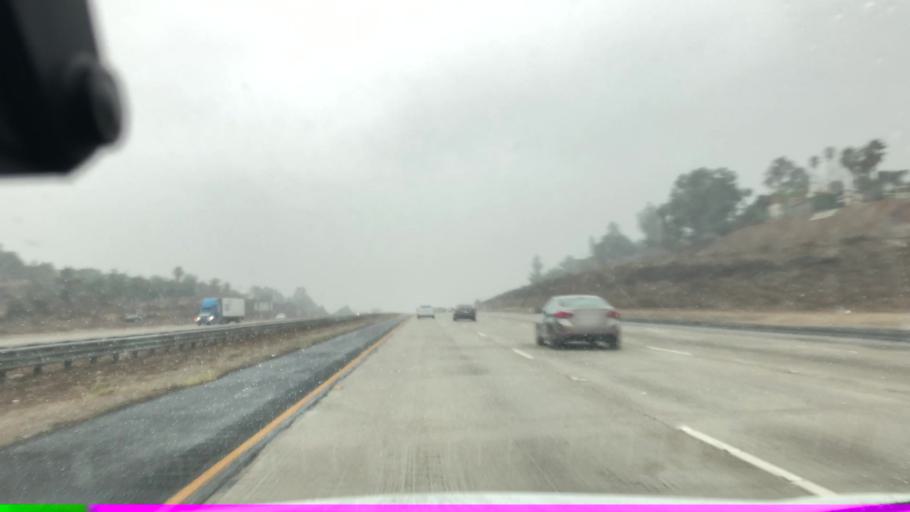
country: US
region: California
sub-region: San Diego County
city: Hidden Meadows
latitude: 33.1908
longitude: -117.1222
